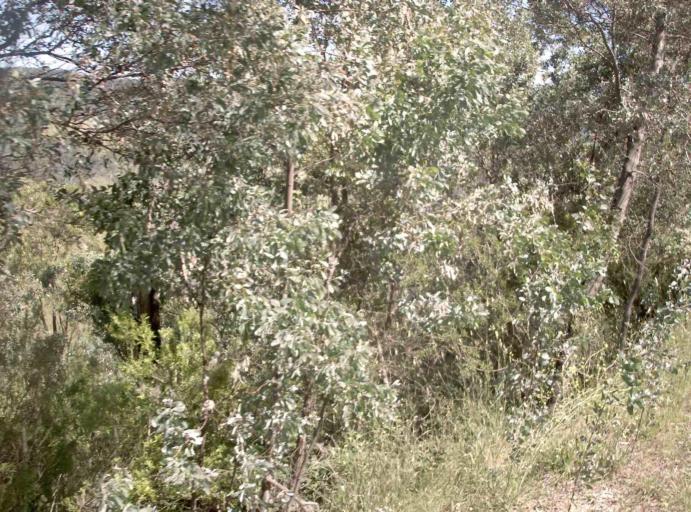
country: AU
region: Victoria
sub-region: East Gippsland
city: Lakes Entrance
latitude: -37.4754
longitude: 148.1851
